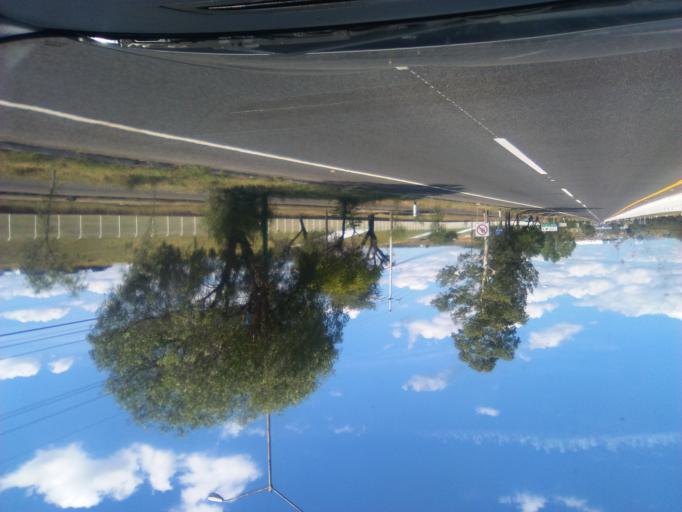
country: MX
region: Guanajuato
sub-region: Silao de la Victoria
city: Aguas Buenas
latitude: 20.9529
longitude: -101.3810
